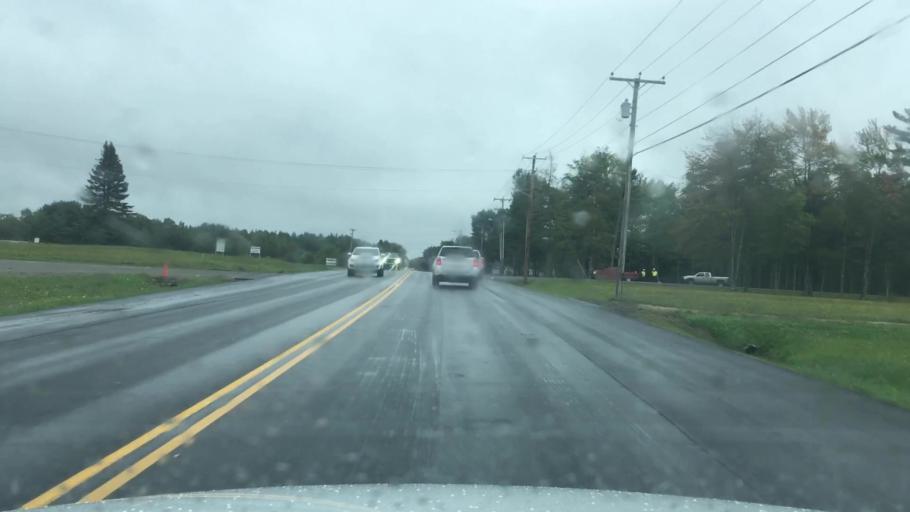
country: US
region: Maine
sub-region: Penobscot County
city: Hampden
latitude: 44.7668
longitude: -68.8546
